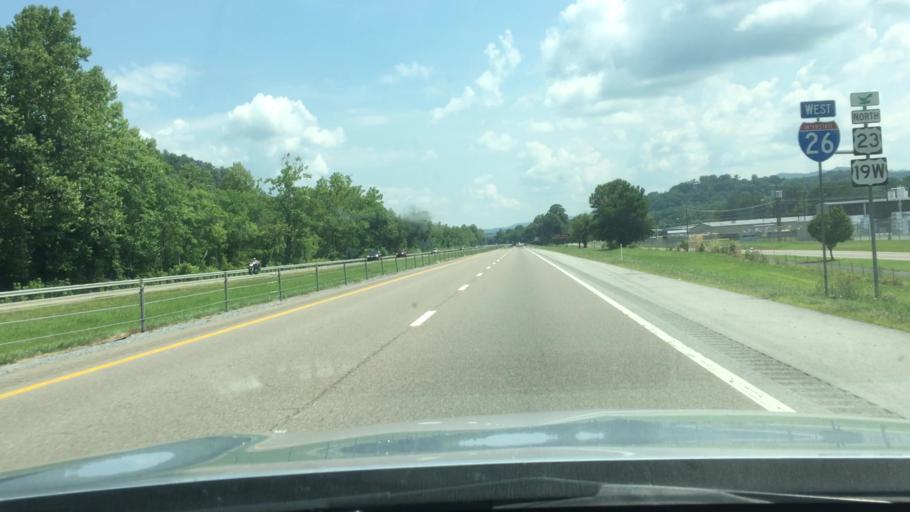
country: US
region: Tennessee
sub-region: Unicoi County
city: Banner Hill
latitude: 36.1289
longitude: -82.4409
